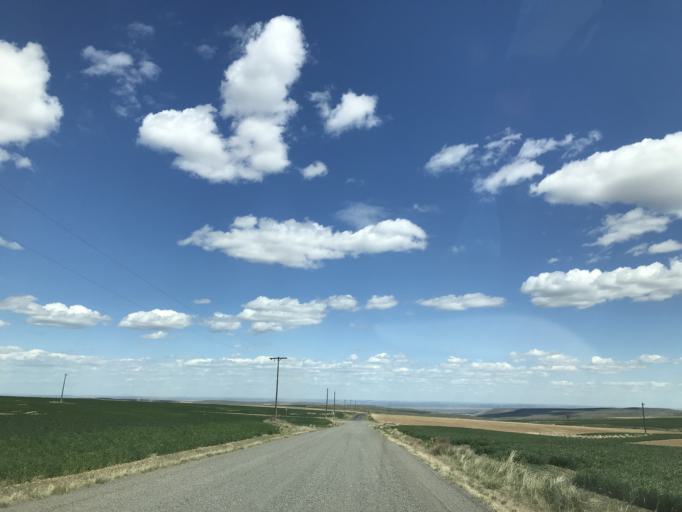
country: US
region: Washington
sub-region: Grant County
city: Ephrata
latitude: 47.3375
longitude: -119.7073
